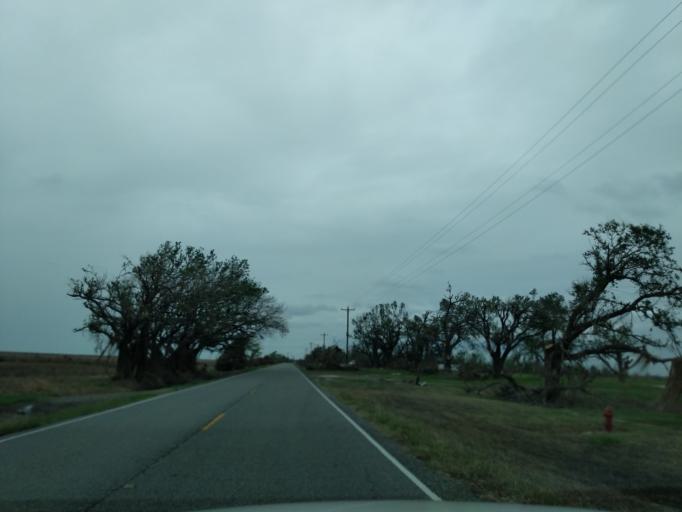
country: US
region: Louisiana
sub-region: Cameron Parish
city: Cameron
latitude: 29.7868
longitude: -93.1373
